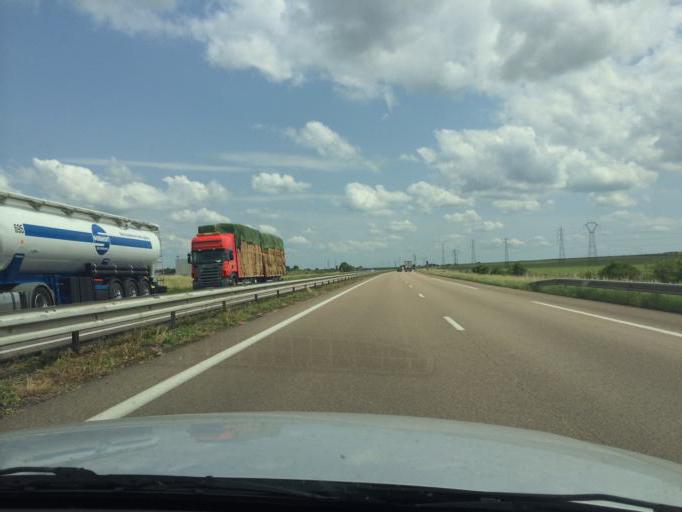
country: FR
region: Champagne-Ardenne
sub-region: Departement de la Marne
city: Sillery
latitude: 49.1888
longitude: 4.1404
